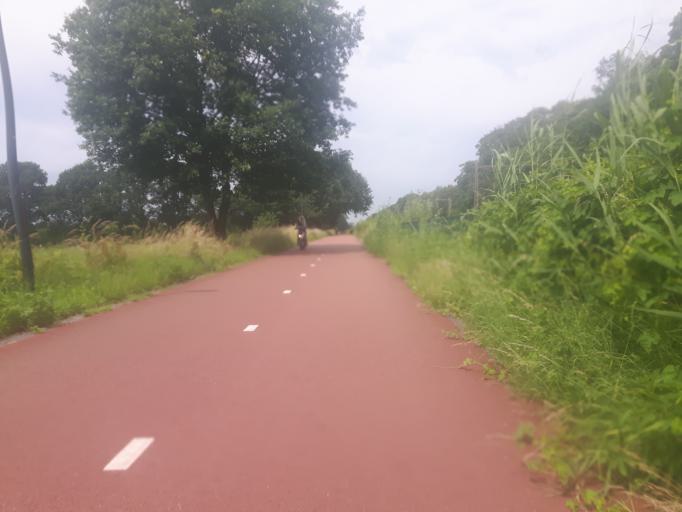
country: NL
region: Overijssel
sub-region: Gemeente Hengelo
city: Hengelo
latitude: 52.2495
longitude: 6.8193
